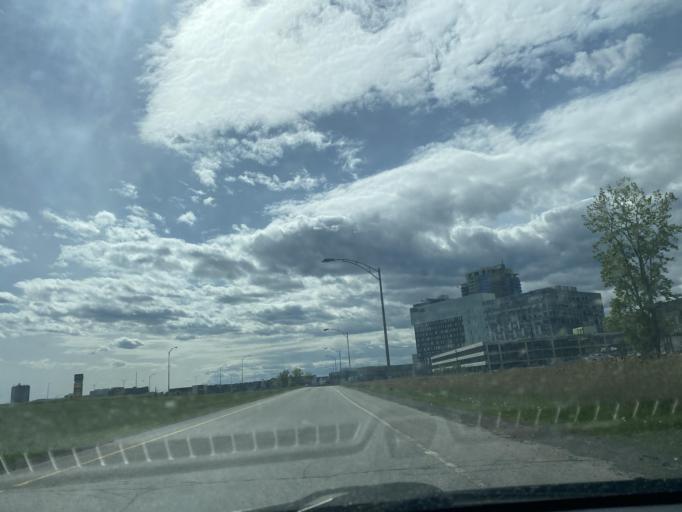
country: CA
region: Quebec
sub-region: Monteregie
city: Brossard
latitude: 45.4466
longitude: -73.4265
